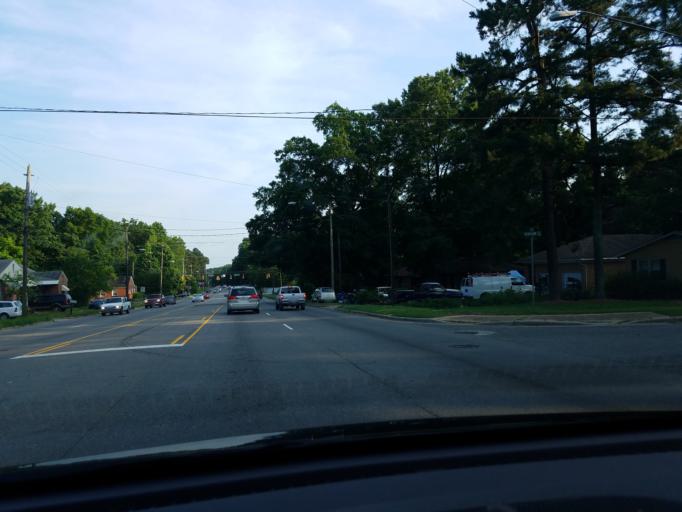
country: US
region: North Carolina
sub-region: Durham County
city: Durham
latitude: 36.0418
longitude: -78.9059
